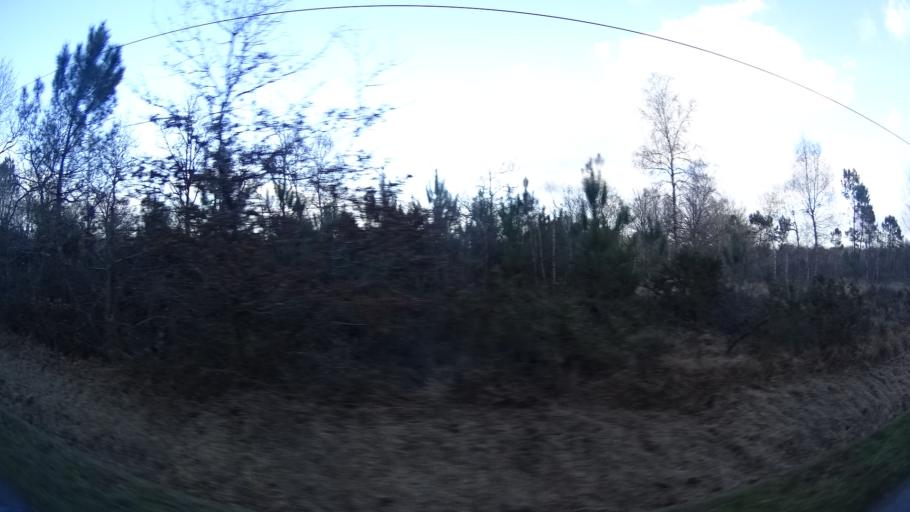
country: FR
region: Pays de la Loire
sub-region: Departement de la Loire-Atlantique
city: Guenrouet
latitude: 47.5686
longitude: -1.9735
